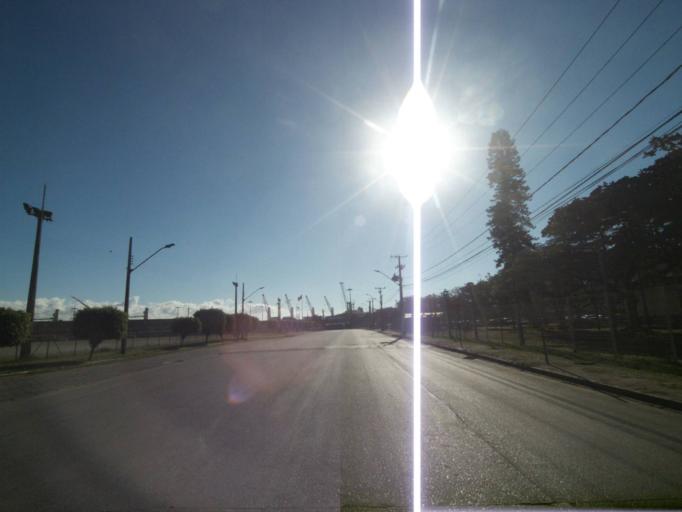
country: BR
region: Parana
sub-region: Paranagua
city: Paranagua
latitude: -25.5060
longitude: -48.5158
